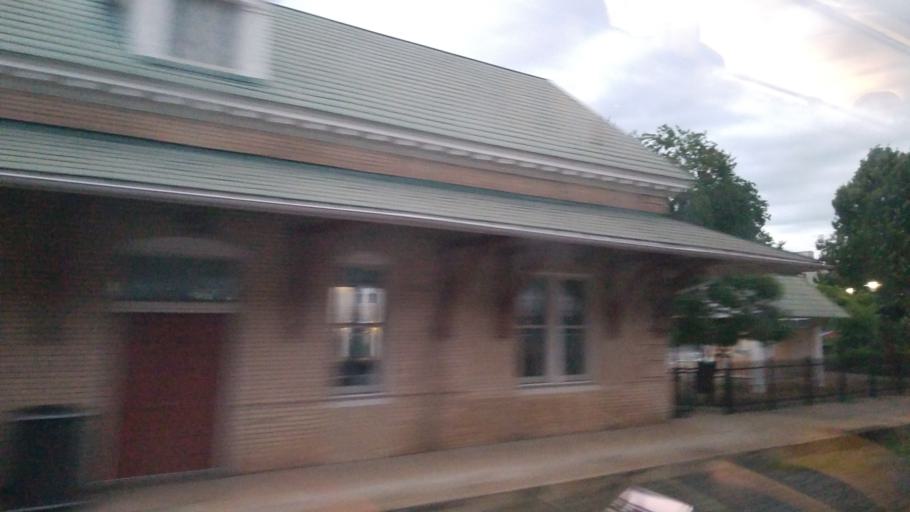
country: US
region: Virginia
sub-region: Orange County
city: Orange
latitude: 38.2452
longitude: -78.1101
